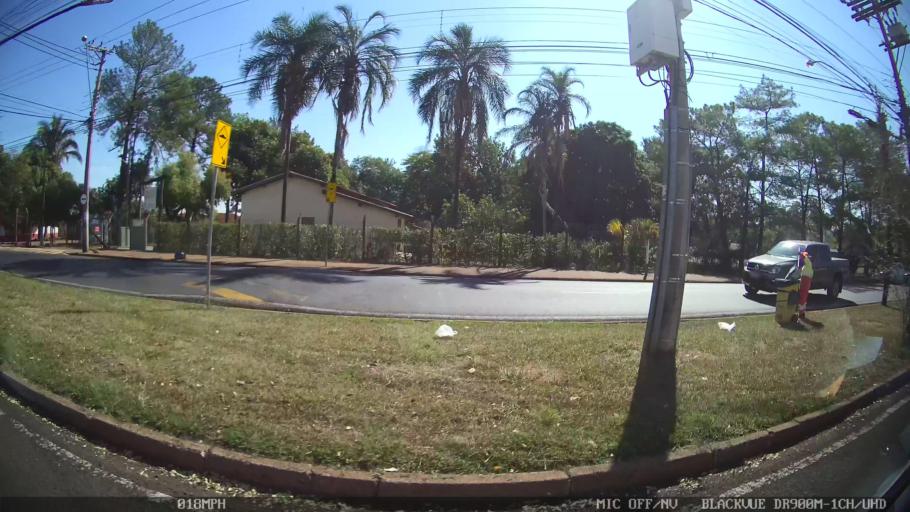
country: BR
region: Sao Paulo
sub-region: Sao Jose Do Rio Preto
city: Sao Jose do Rio Preto
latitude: -20.8102
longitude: -49.4108
